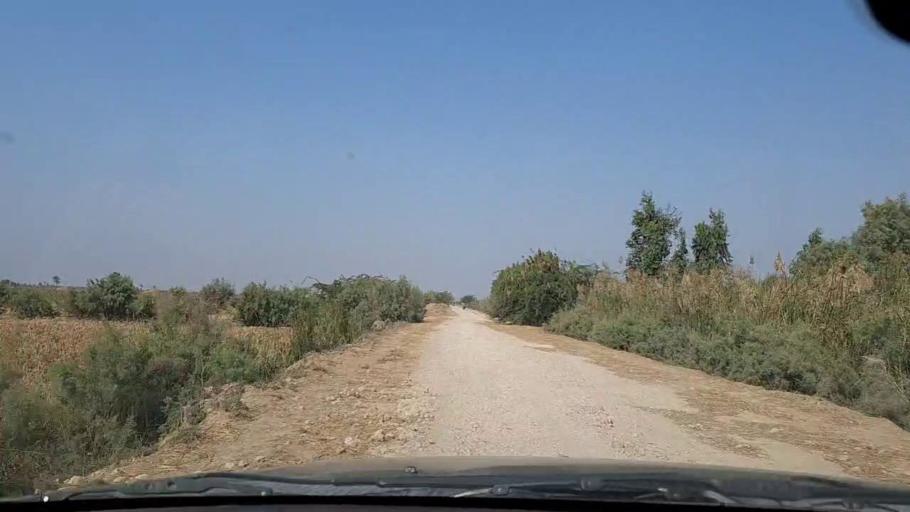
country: PK
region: Sindh
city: Mirpur Sakro
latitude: 24.3502
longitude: 67.6831
